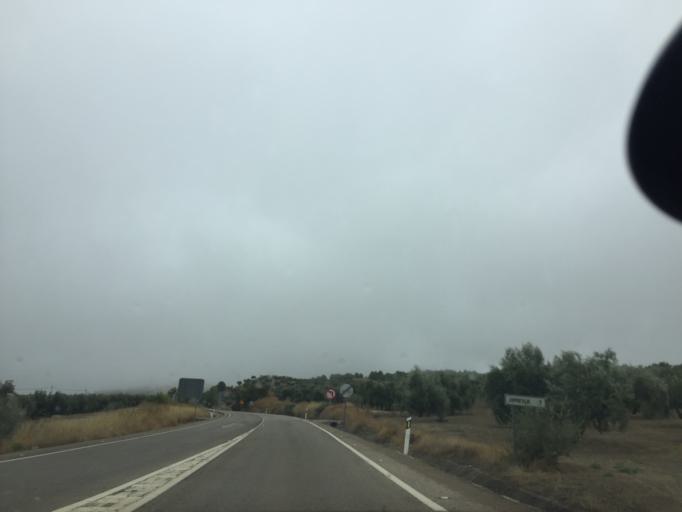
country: ES
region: Andalusia
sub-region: Provincia de Jaen
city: Jimena
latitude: 37.8401
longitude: -3.5285
